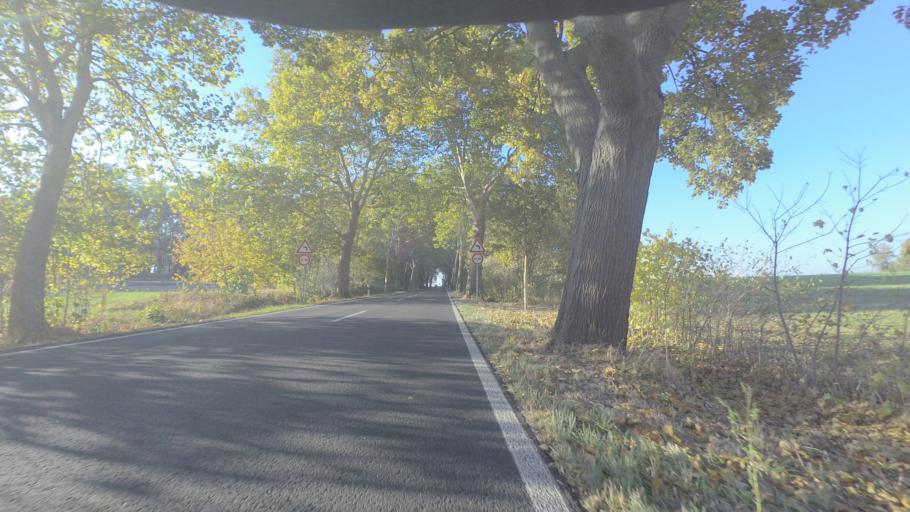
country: DE
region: Brandenburg
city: Zossen
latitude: 52.2507
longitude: 13.4824
